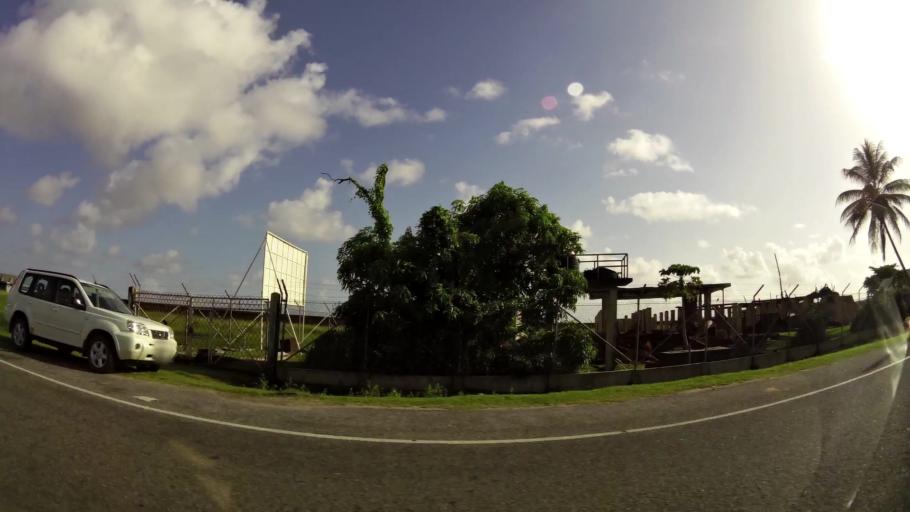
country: GY
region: Demerara-Mahaica
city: Georgetown
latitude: 6.8263
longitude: -58.1229
